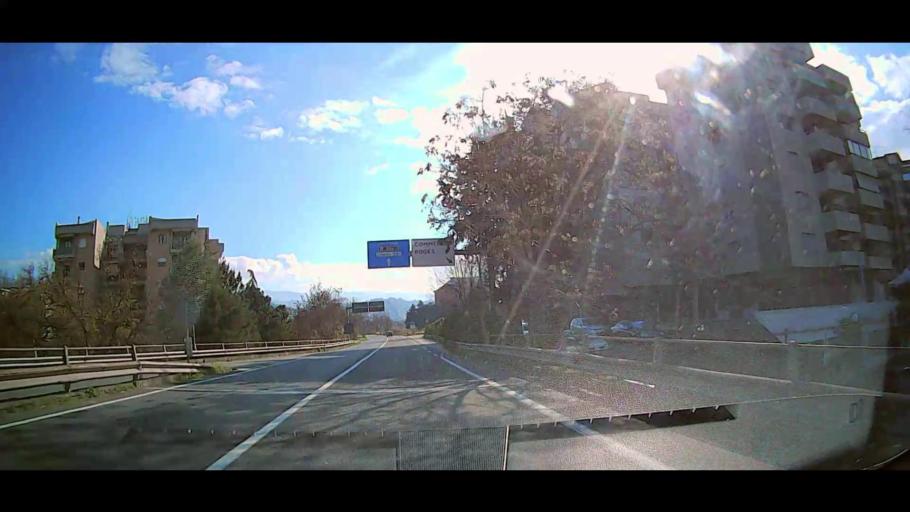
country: IT
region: Calabria
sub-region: Provincia di Cosenza
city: Quattromiglia
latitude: 39.3312
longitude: 16.2453
